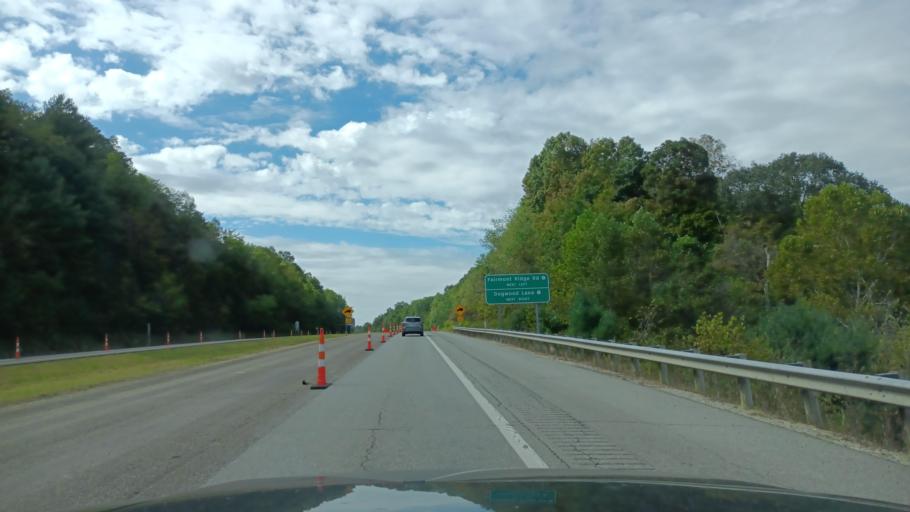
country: US
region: West Virginia
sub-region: Ritchie County
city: Harrisville
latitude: 39.2610
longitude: -81.0868
